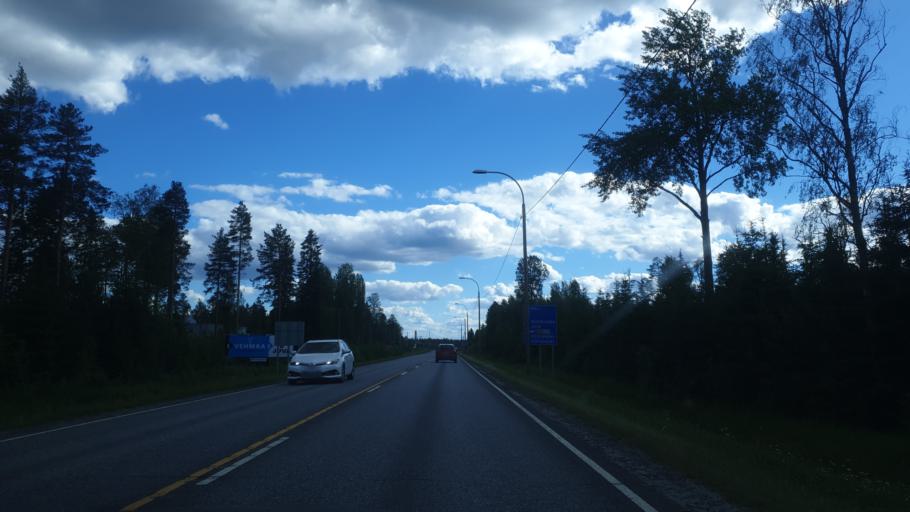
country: FI
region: Southern Savonia
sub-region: Pieksaemaeki
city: Juva
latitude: 61.9070
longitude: 27.8049
